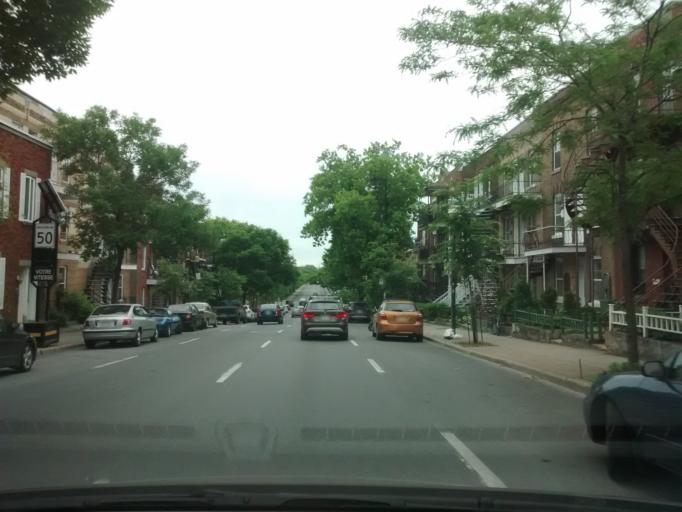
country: CA
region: Quebec
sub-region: Montreal
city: Montreal
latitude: 45.5346
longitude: -73.5584
